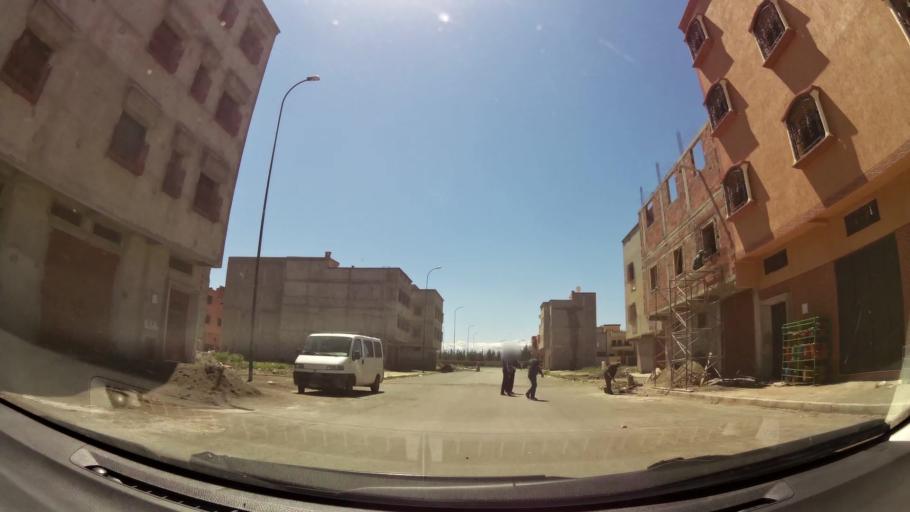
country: MA
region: Marrakech-Tensift-Al Haouz
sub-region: Marrakech
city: Marrakesh
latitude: 31.5514
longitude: -7.9780
